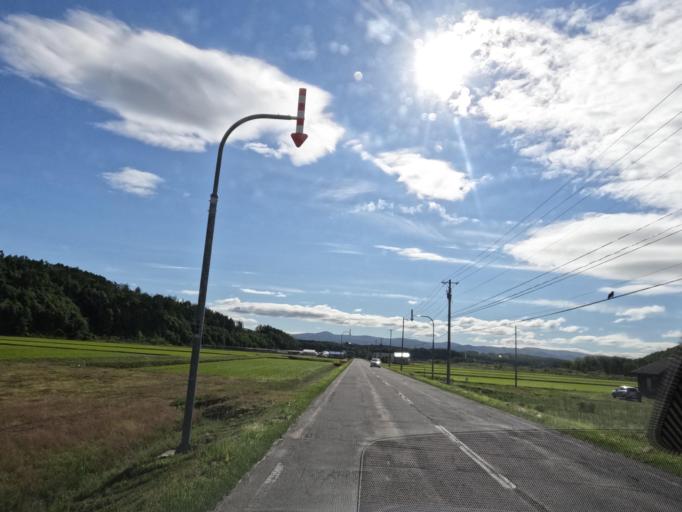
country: JP
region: Hokkaido
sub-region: Asahikawa-shi
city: Asahikawa
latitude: 43.6204
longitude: 142.4923
